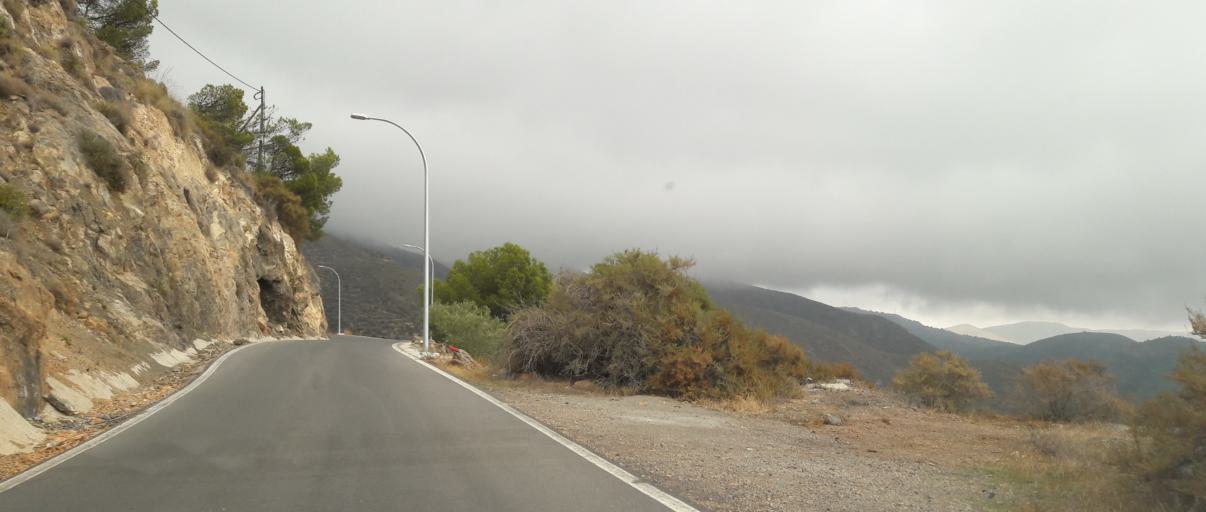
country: ES
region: Andalusia
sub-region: Provincia de Almeria
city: Vicar
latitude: 36.8698
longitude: -2.6543
